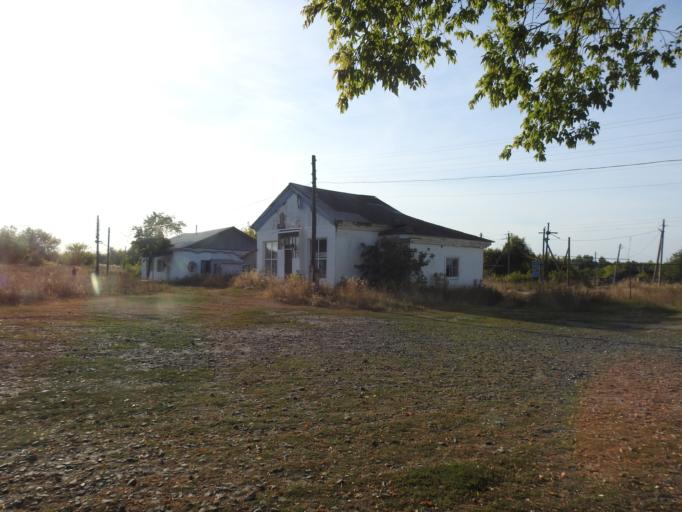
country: RU
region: Saratov
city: Novyye Burasy
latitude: 52.2101
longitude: 46.1233
